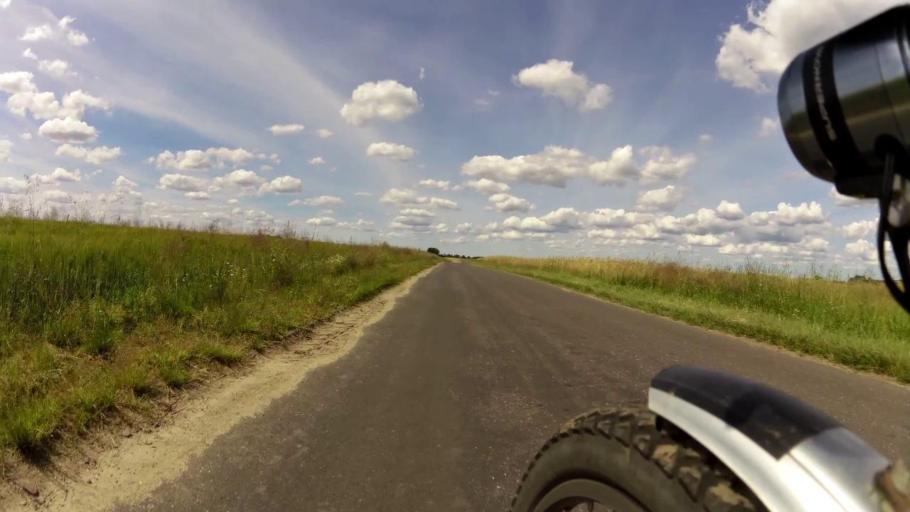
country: PL
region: West Pomeranian Voivodeship
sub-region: Powiat stargardzki
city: Chociwel
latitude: 53.5402
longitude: 15.4307
